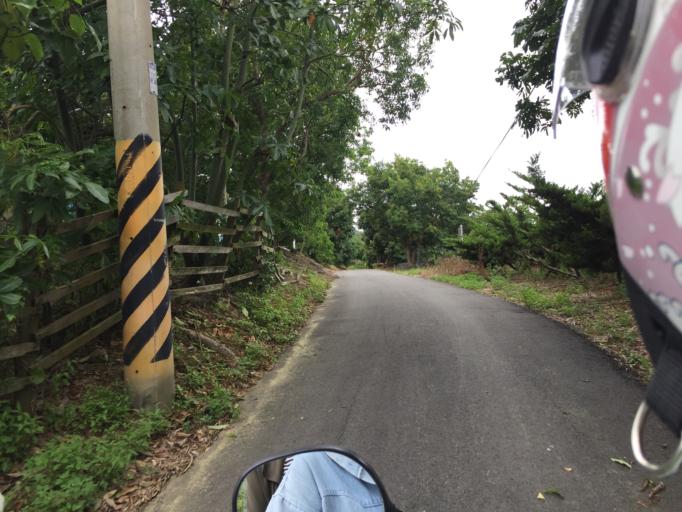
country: TW
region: Taiwan
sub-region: Taichung City
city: Taichung
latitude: 24.0642
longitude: 120.7176
